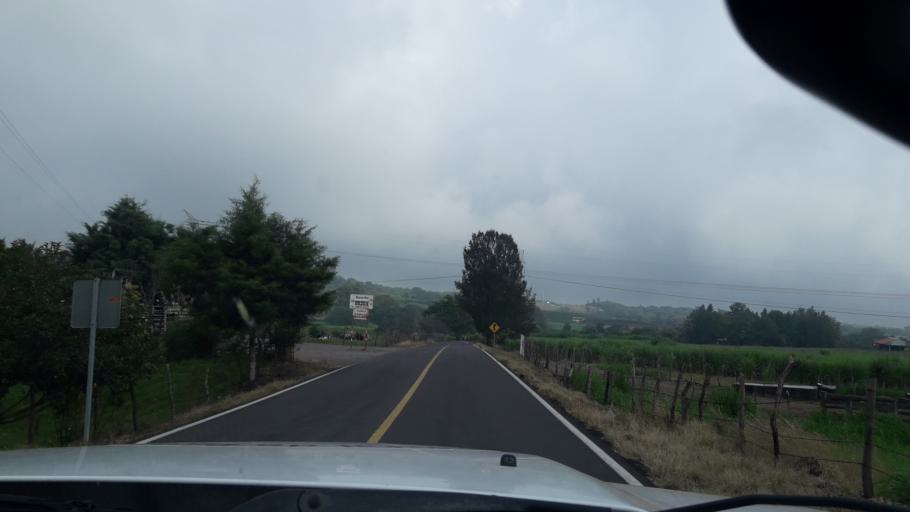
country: MX
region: Colima
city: Queseria
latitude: 19.4098
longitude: -103.6426
